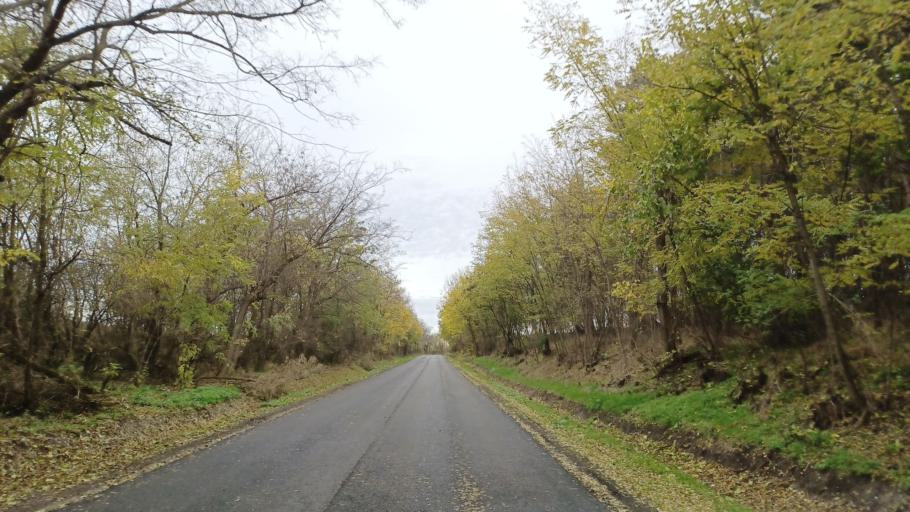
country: HU
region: Tolna
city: Tengelic
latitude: 46.5346
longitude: 18.7600
